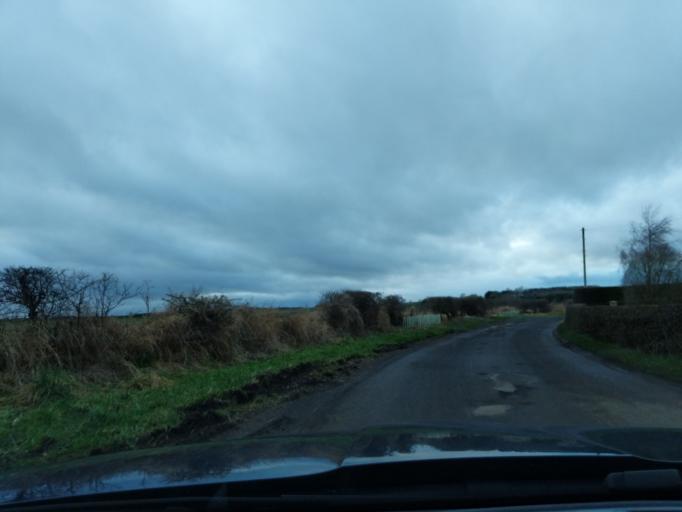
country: GB
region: England
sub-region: Northumberland
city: Ancroft
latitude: 55.7014
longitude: -2.0168
